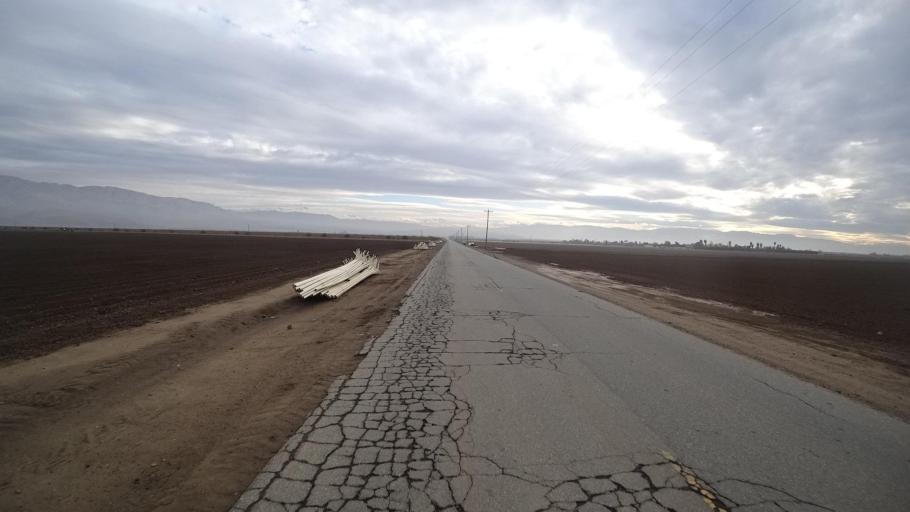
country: US
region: California
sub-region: Kern County
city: Arvin
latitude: 35.1845
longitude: -118.8240
